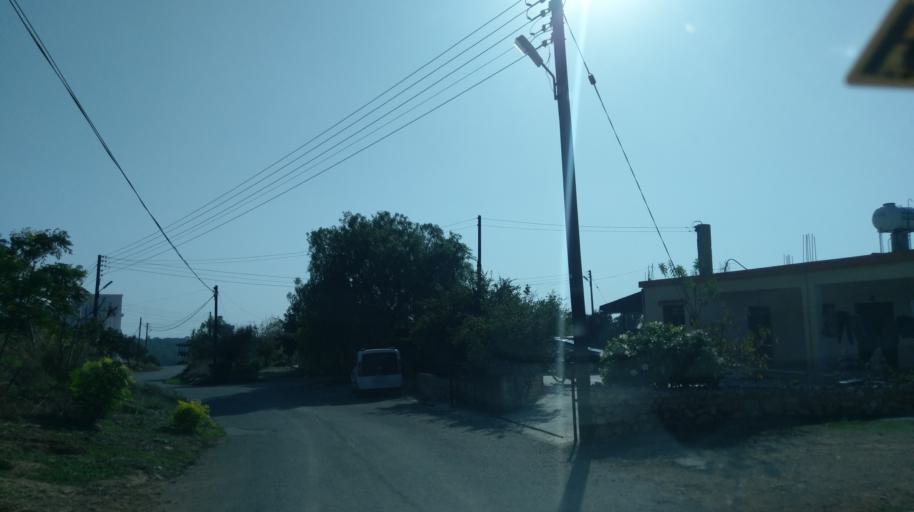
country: CY
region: Ammochostos
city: Leonarisso
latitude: 35.4795
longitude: 34.1875
